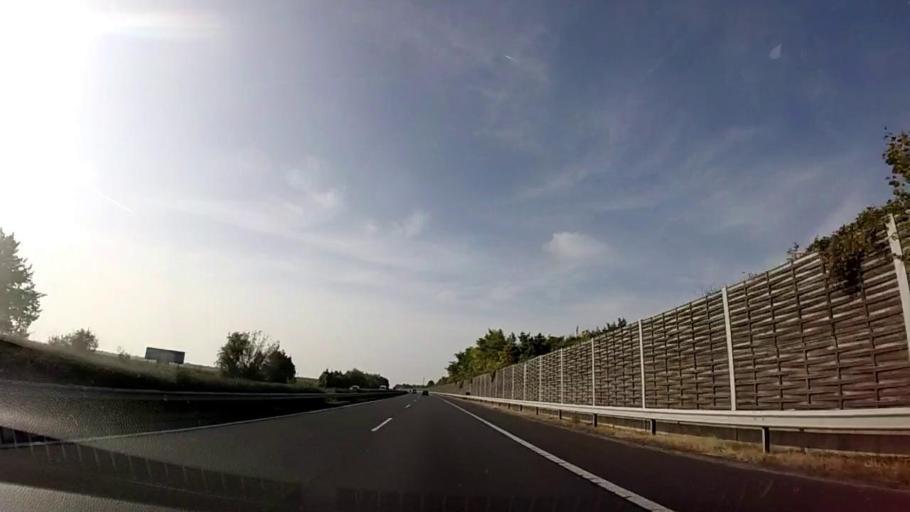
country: HU
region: Fejer
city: Lepseny
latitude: 46.9845
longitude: 18.1790
